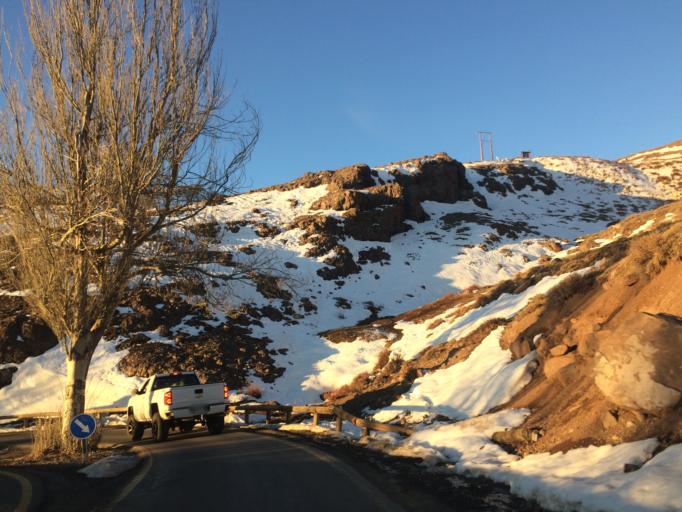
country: CL
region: Santiago Metropolitan
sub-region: Provincia de Santiago
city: Villa Presidente Frei, Nunoa, Santiago, Chile
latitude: -33.3407
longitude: -70.2938
